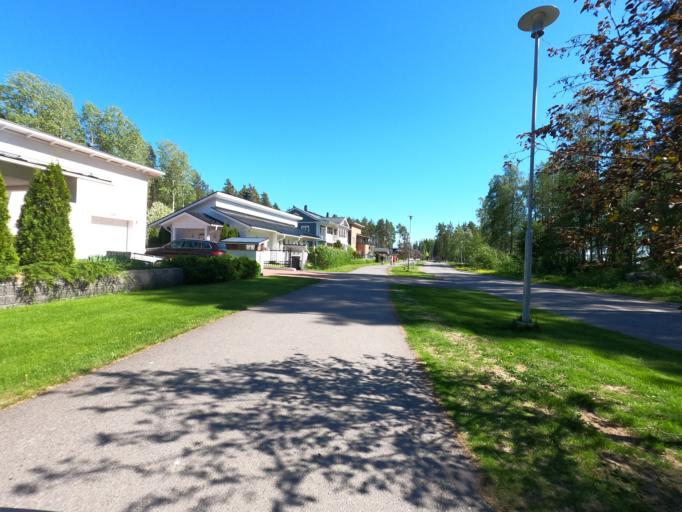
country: FI
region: North Karelia
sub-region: Joensuu
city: Joensuu
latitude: 62.5779
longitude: 29.7658
